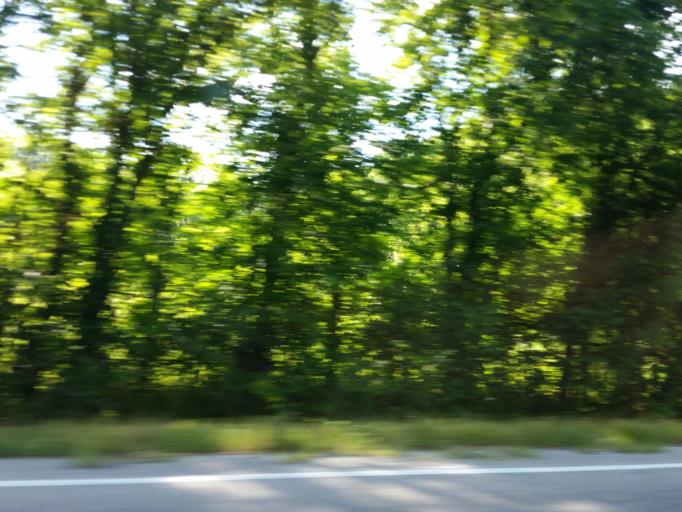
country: US
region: Tennessee
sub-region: Maury County
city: Mount Pleasant
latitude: 35.5782
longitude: -87.3214
